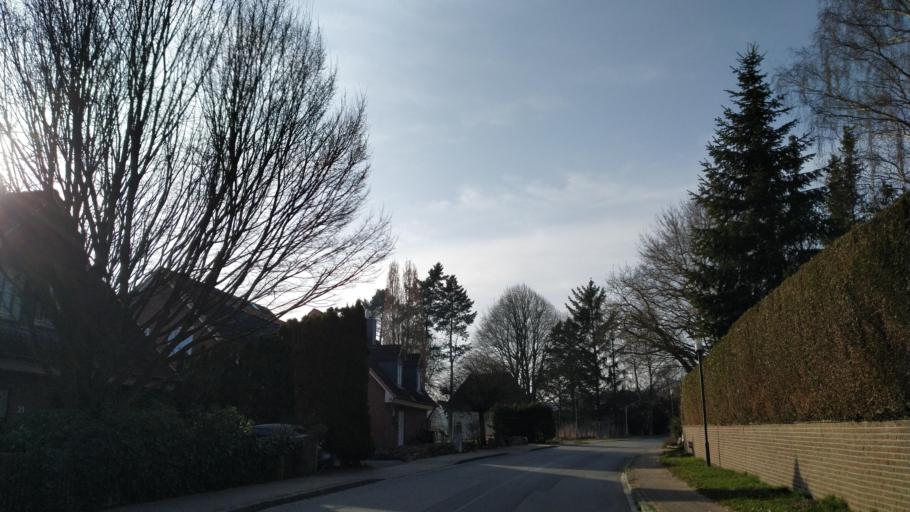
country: DE
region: Schleswig-Holstein
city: Bad Schwartau
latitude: 53.9402
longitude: 10.6903
